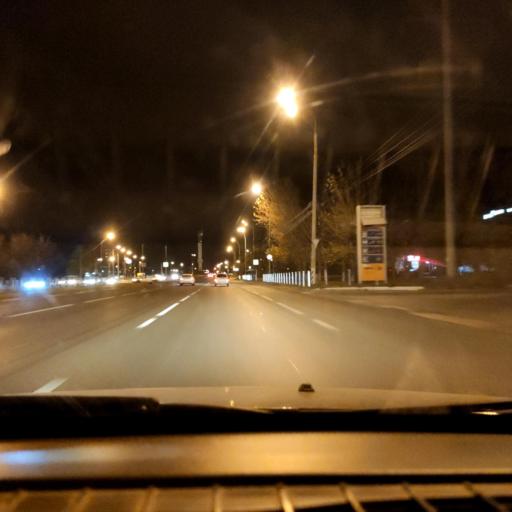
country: RU
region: Samara
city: Tol'yatti
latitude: 53.5501
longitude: 49.2870
